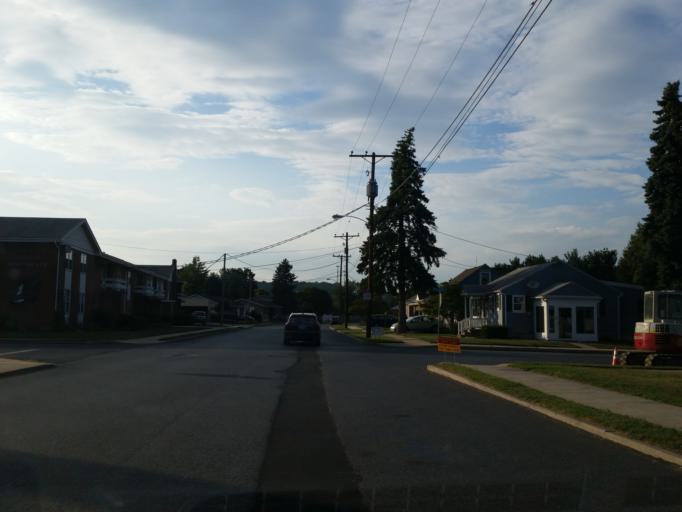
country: US
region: Pennsylvania
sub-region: Lebanon County
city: Palmyra
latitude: 40.3127
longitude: -76.5877
